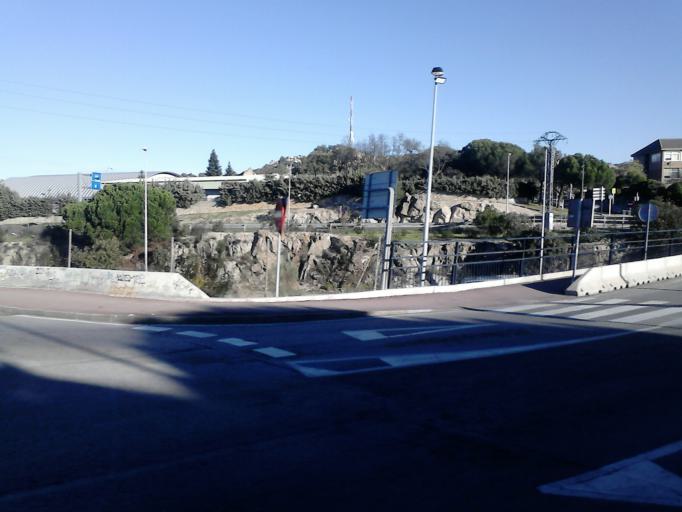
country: ES
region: Madrid
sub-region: Provincia de Madrid
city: Torrelodones
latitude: 40.5775
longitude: -3.9390
